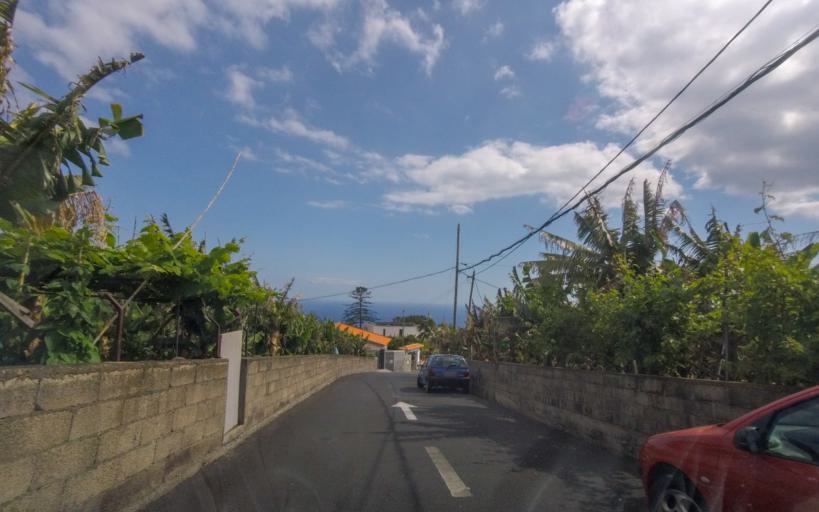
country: PT
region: Madeira
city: Camara de Lobos
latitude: 32.6493
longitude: -16.9507
